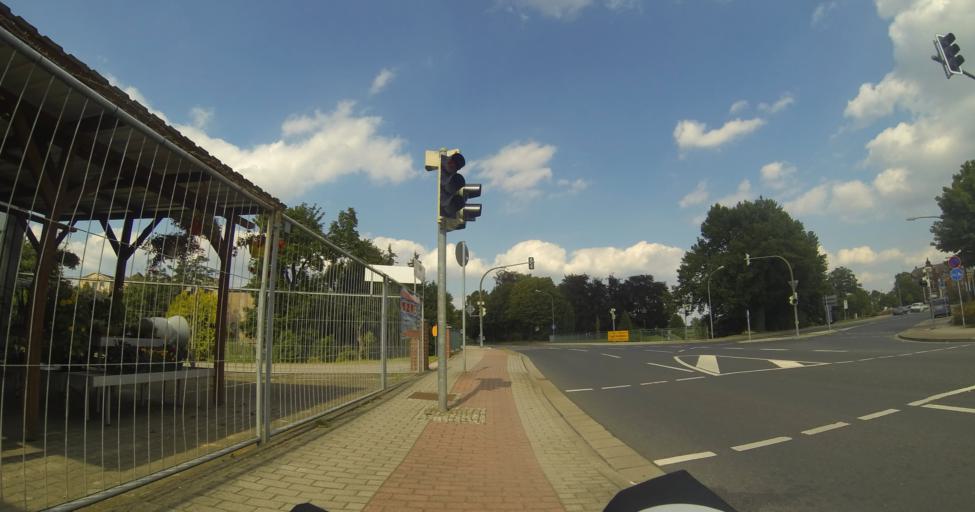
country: DE
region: Saxony
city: Grossenhain
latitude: 51.2865
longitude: 13.5311
